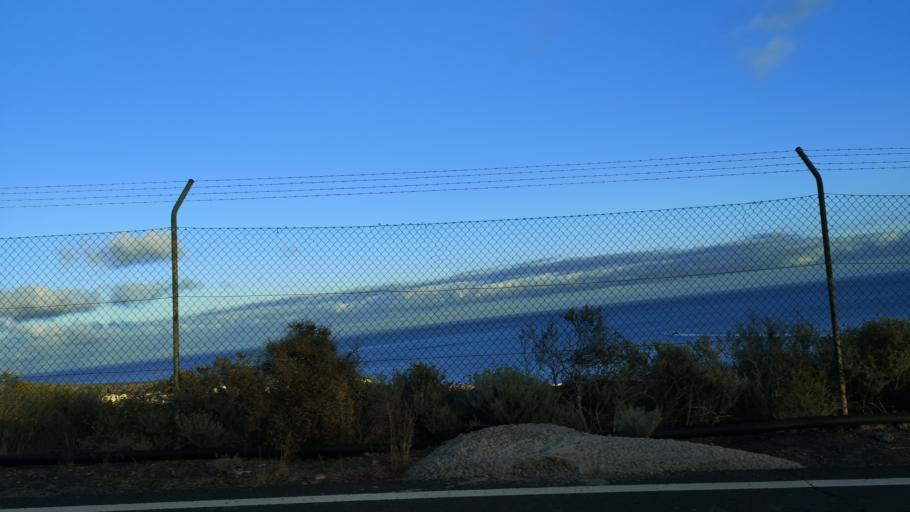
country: ES
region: Canary Islands
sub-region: Provincia de Santa Cruz de Tenerife
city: Alajero
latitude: 28.0300
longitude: -17.2058
